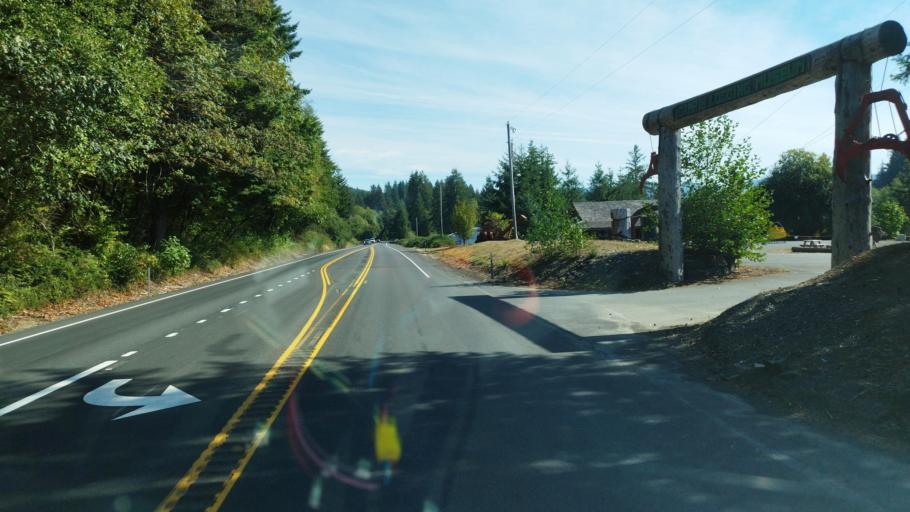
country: US
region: Oregon
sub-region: Clatsop County
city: Seaside
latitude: 45.8865
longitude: -123.6141
